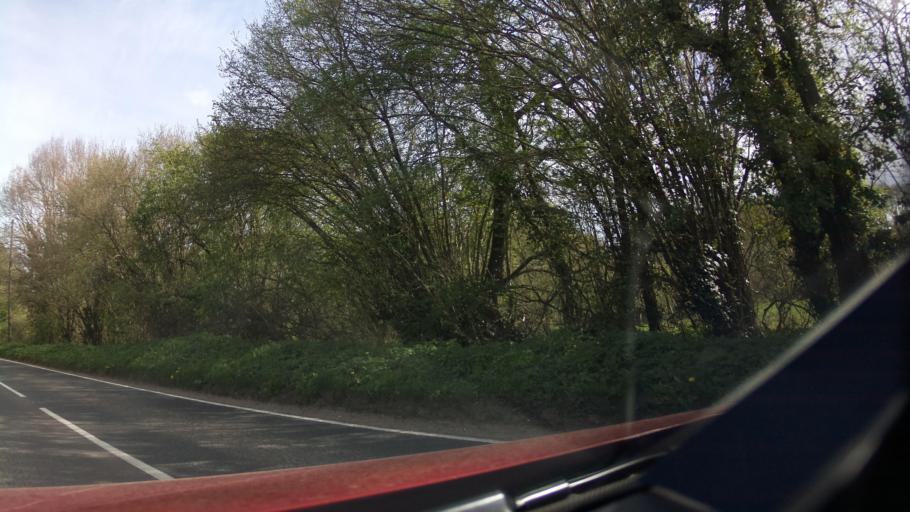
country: GB
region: England
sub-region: Hampshire
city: Compton
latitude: 51.0144
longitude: -1.3542
